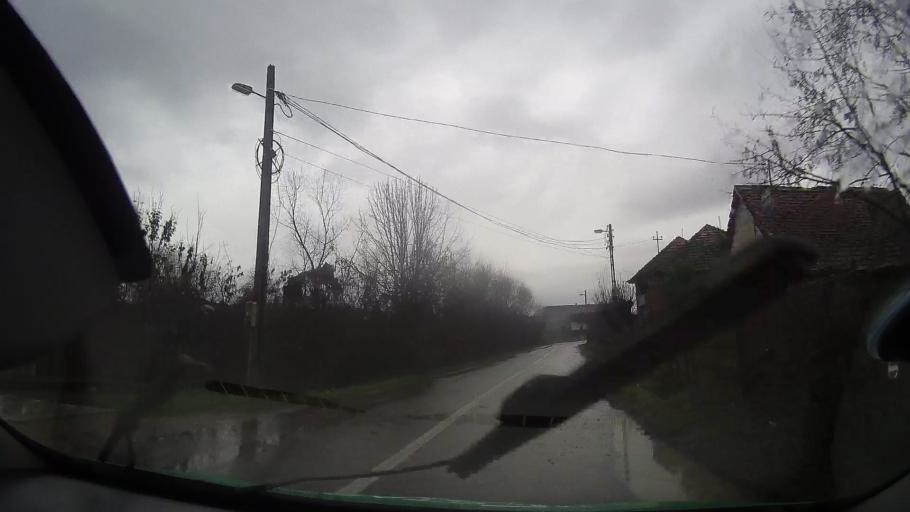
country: RO
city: Capalna
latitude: 46.7181
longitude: 22.0810
